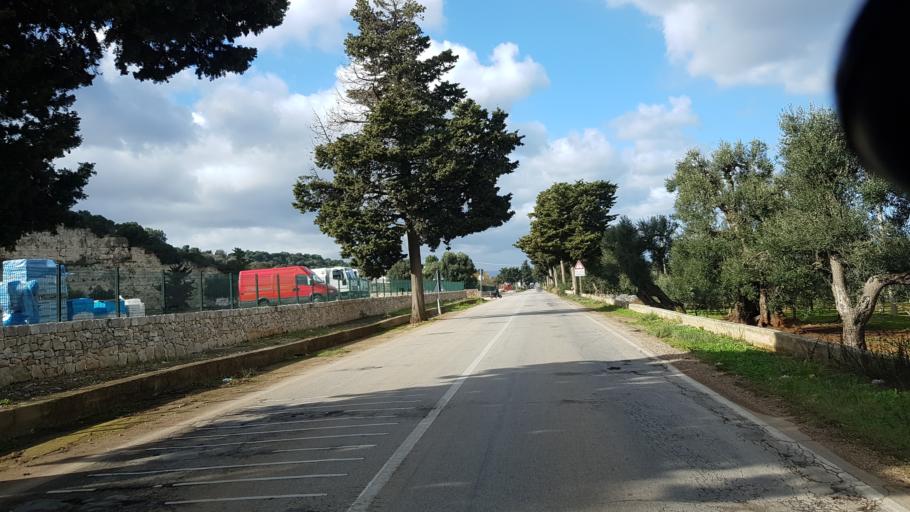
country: IT
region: Apulia
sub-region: Provincia di Brindisi
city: Ostuni
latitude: 40.7480
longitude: 17.5568
